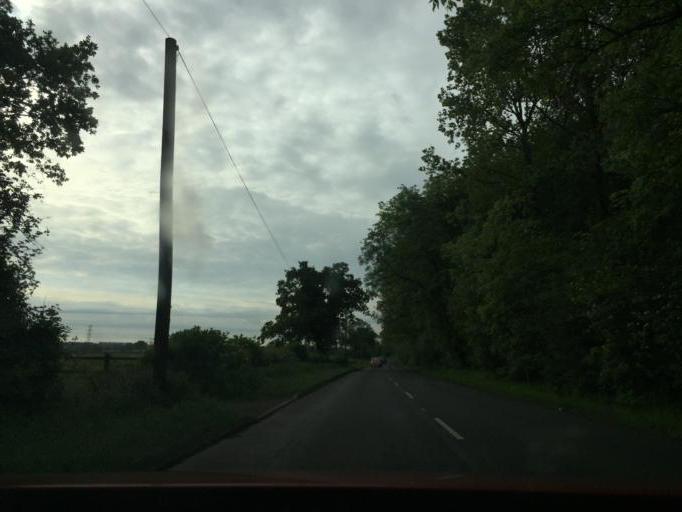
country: GB
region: England
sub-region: Leicestershire
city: Sapcote
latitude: 52.4660
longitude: -1.3032
